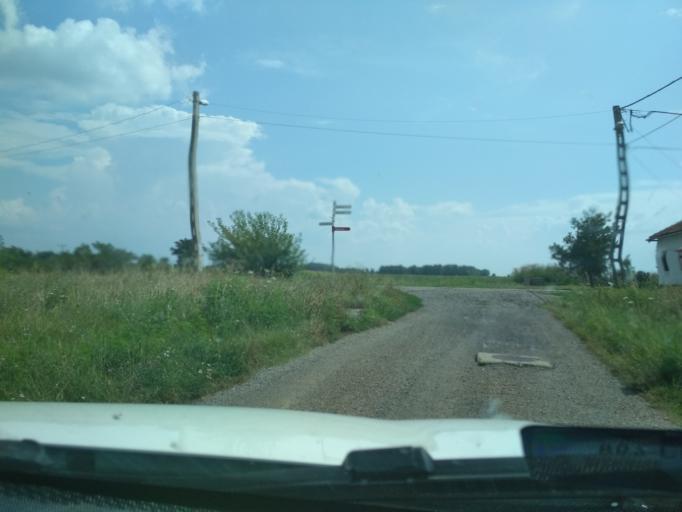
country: HU
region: Jasz-Nagykun-Szolnok
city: Abadszalok
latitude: 47.4689
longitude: 20.5840
